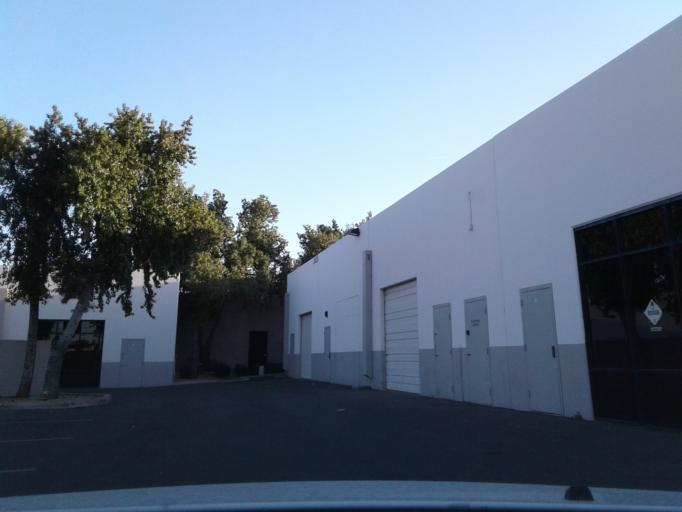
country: US
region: Arizona
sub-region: Maricopa County
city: Glendale
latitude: 33.5708
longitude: -112.1106
